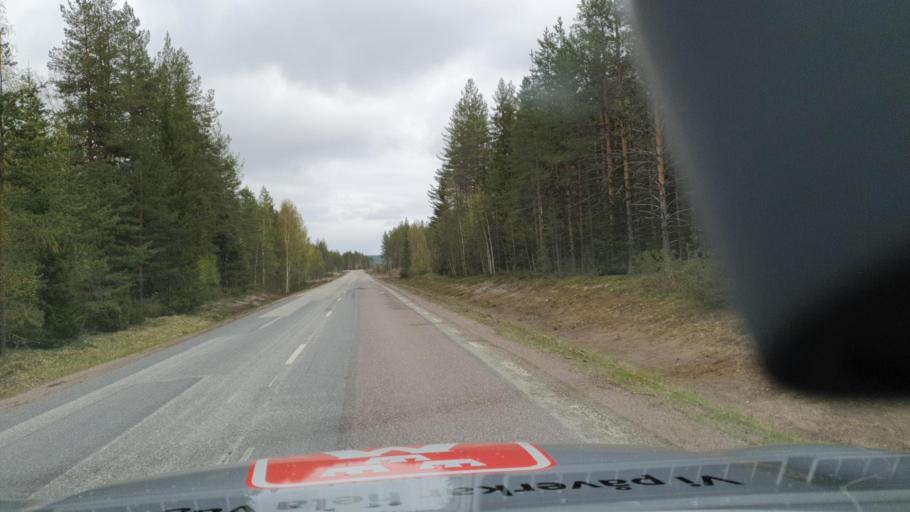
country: SE
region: Vaesternorrland
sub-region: Solleftea Kommun
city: Solleftea
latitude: 63.6524
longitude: 17.3446
